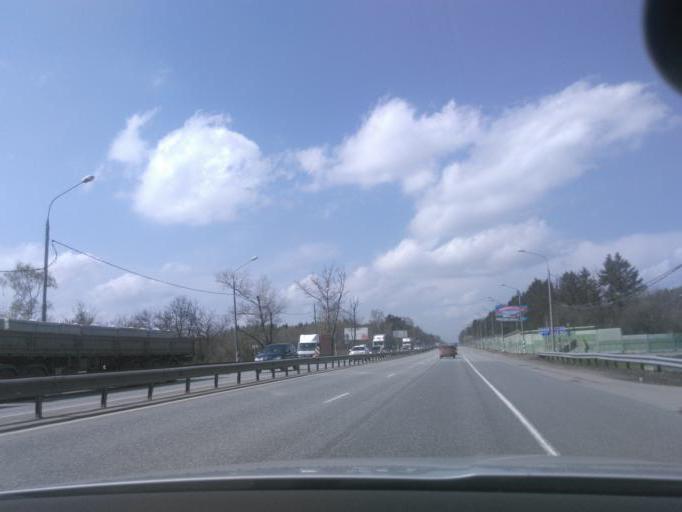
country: RU
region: Moskovskaya
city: Rzhavki
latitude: 56.0032
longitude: 37.2359
